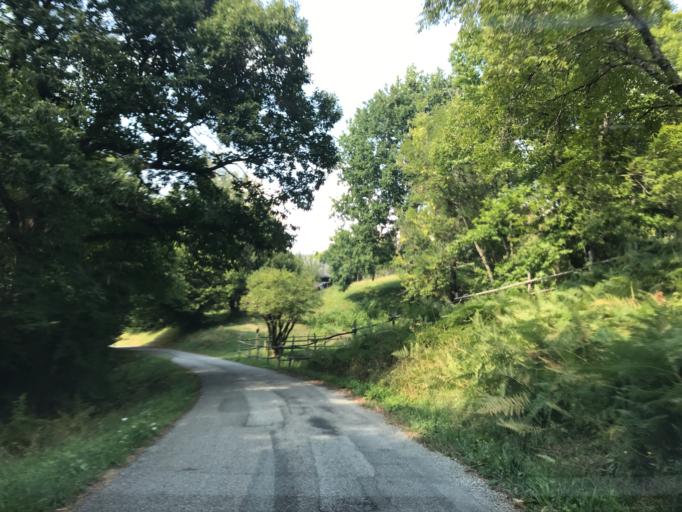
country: FR
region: Rhone-Alpes
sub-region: Departement de la Savoie
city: La Rochette
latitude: 45.4714
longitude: 6.1871
